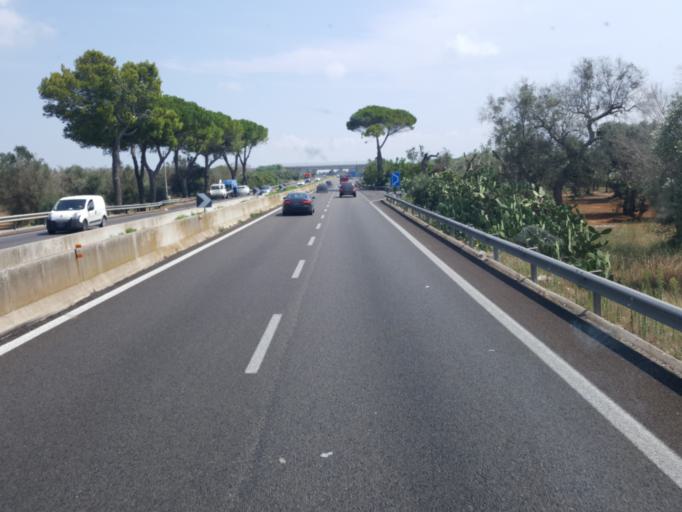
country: IT
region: Apulia
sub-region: Provincia di Lecce
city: Squinzano
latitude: 40.4438
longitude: 18.0749
